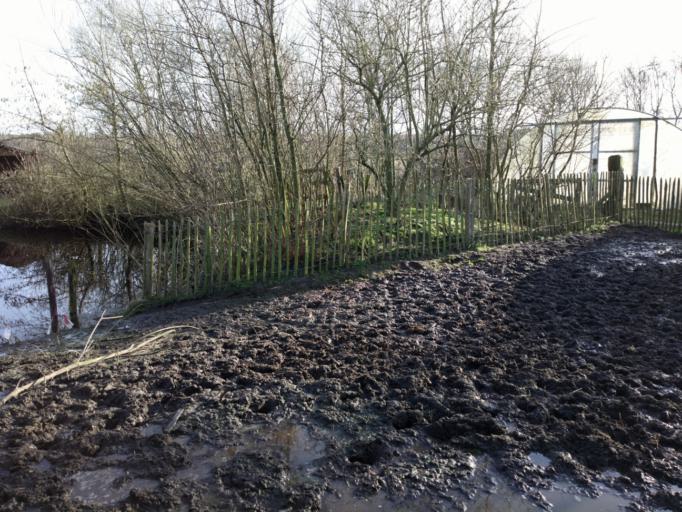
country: NL
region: North Holland
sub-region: Gemeente Texel
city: Den Burg
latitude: 53.0880
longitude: 4.7572
